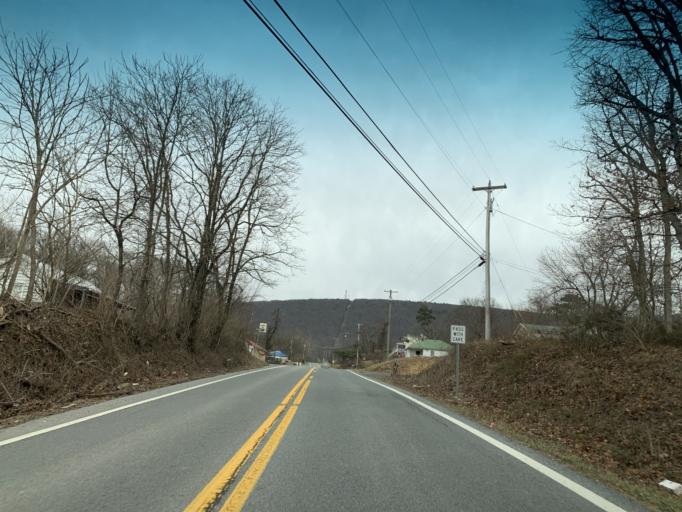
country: US
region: West Virginia
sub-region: Jefferson County
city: Shannondale
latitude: 39.2441
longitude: -77.7908
